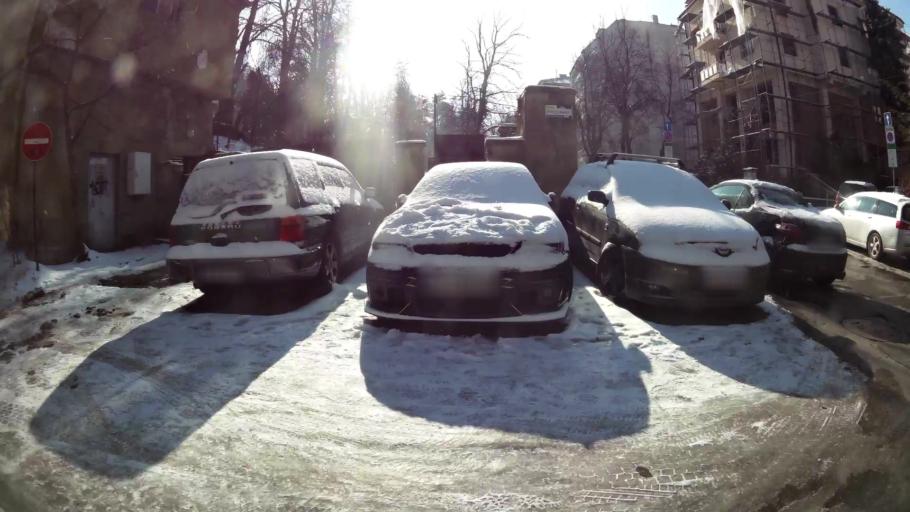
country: BG
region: Sofia-Capital
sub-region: Stolichna Obshtina
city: Sofia
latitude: 42.6773
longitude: 23.3253
